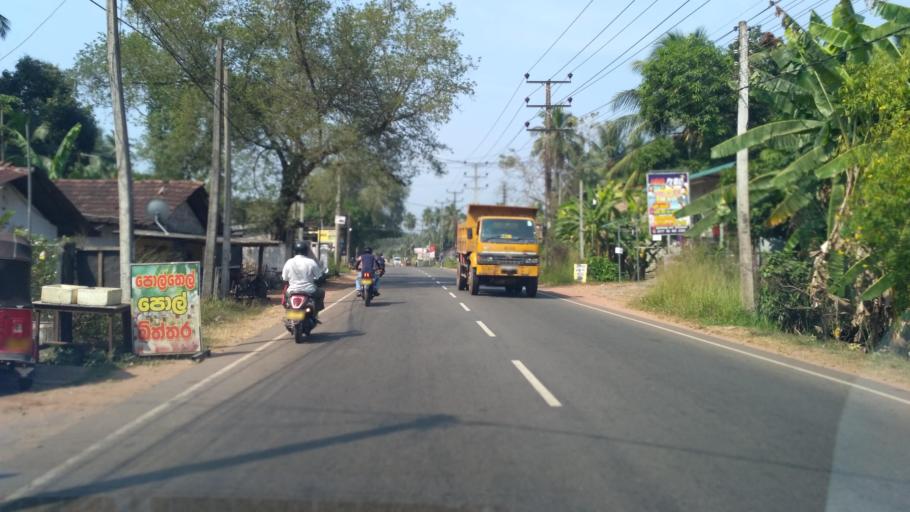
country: LK
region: Western
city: Minuwangoda
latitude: 7.3192
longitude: 79.9662
